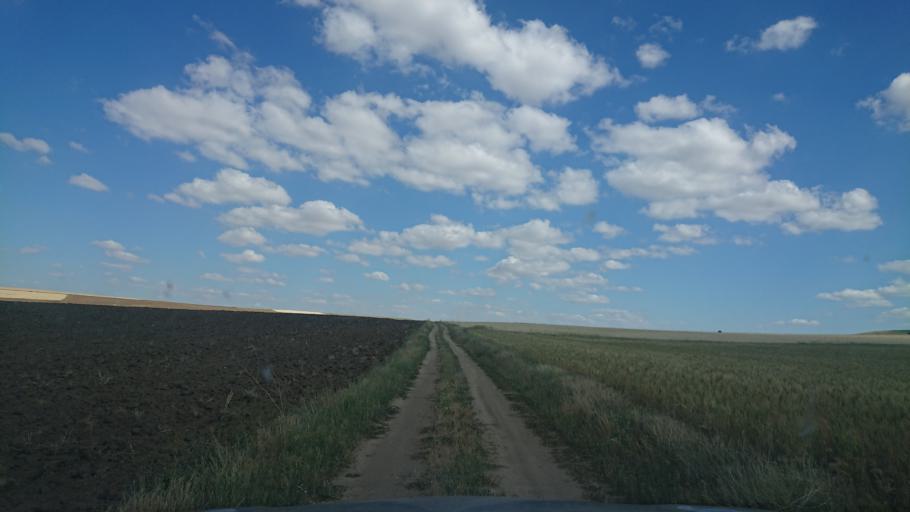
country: TR
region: Aksaray
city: Sariyahsi
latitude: 38.9356
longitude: 33.8413
